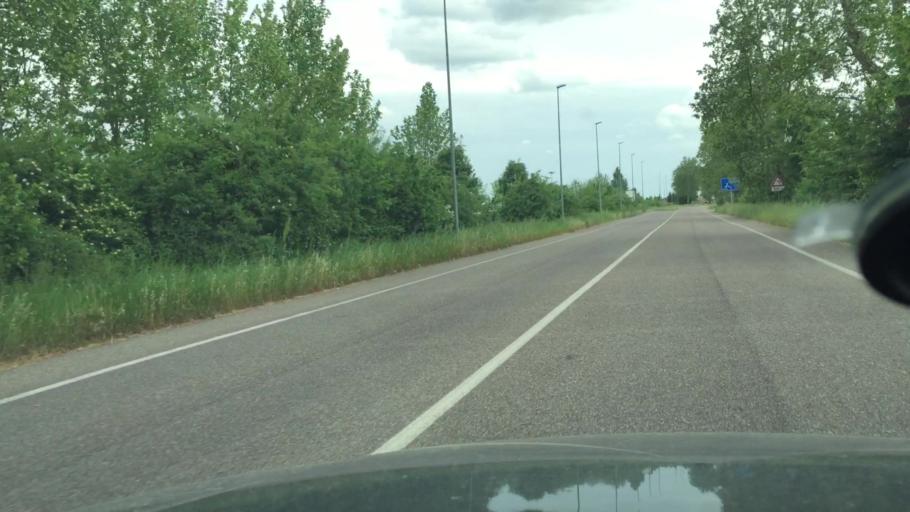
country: IT
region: Emilia-Romagna
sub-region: Provincia di Ferrara
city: Cona
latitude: 44.7999
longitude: 11.7176
